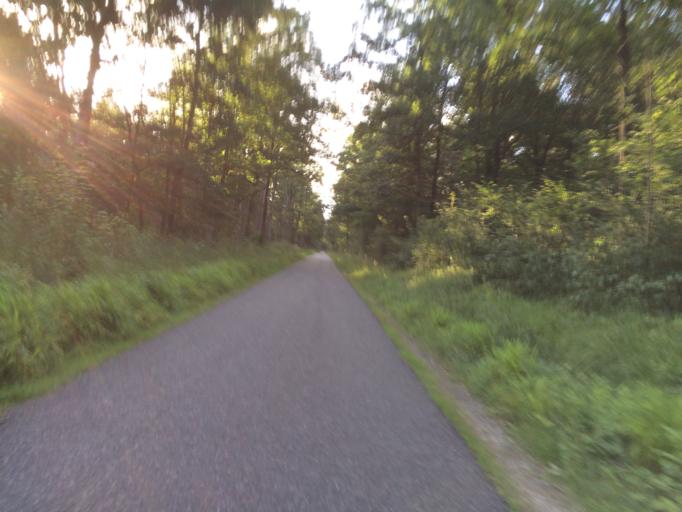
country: FR
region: Ile-de-France
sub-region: Departement de l'Essonne
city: Soisy-sur-Seine
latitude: 48.6651
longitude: 2.4702
